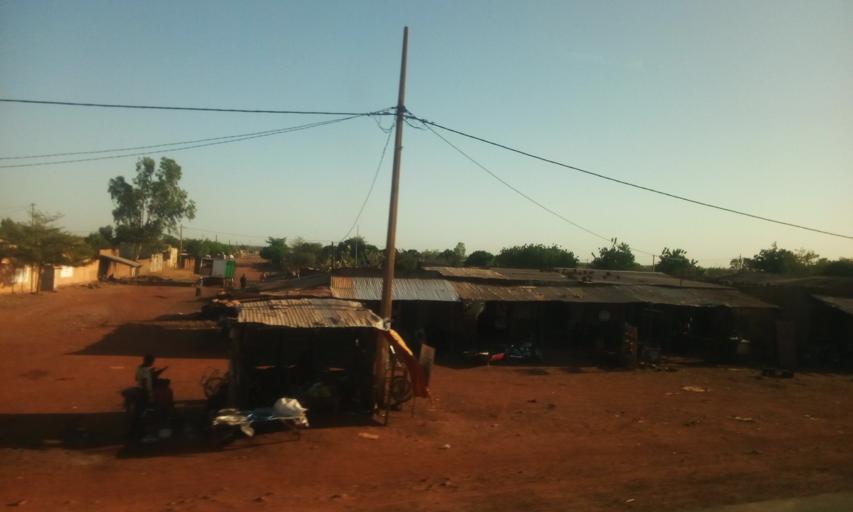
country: ML
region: Segou
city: Baroueli
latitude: 12.7853
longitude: -6.9475
